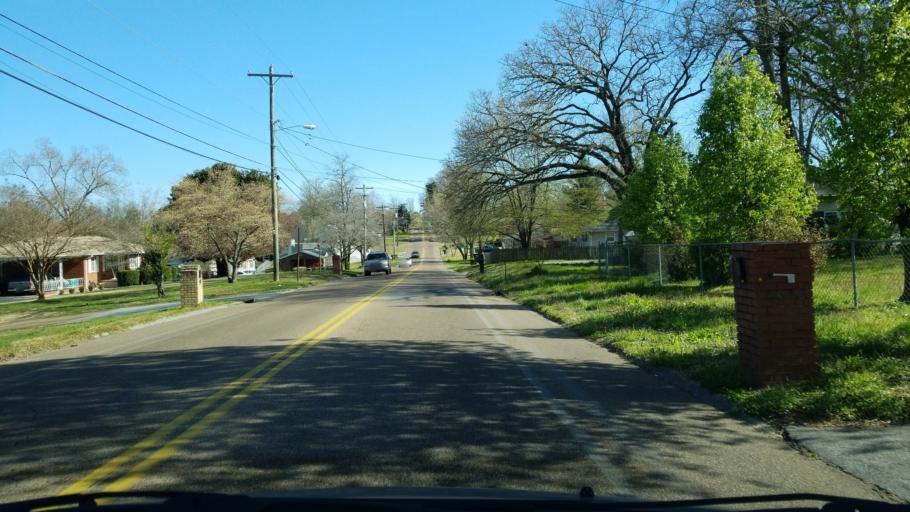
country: US
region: Tennessee
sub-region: Hamilton County
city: Harrison
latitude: 35.0831
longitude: -85.1852
